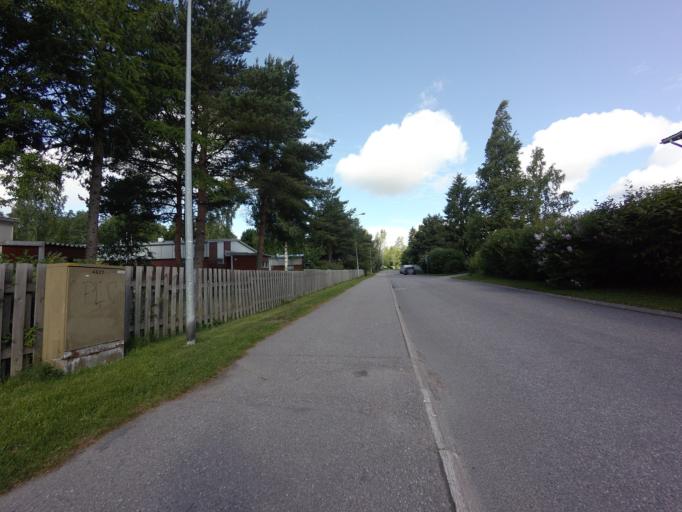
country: FI
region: Uusimaa
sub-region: Helsinki
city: Espoo
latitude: 60.1793
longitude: 24.6708
